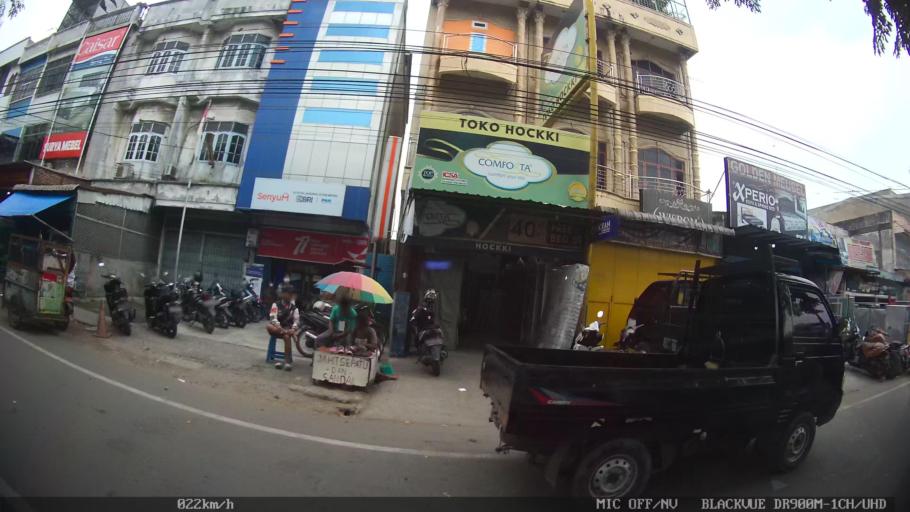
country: ID
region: North Sumatra
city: Medan
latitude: 3.5788
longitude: 98.7035
